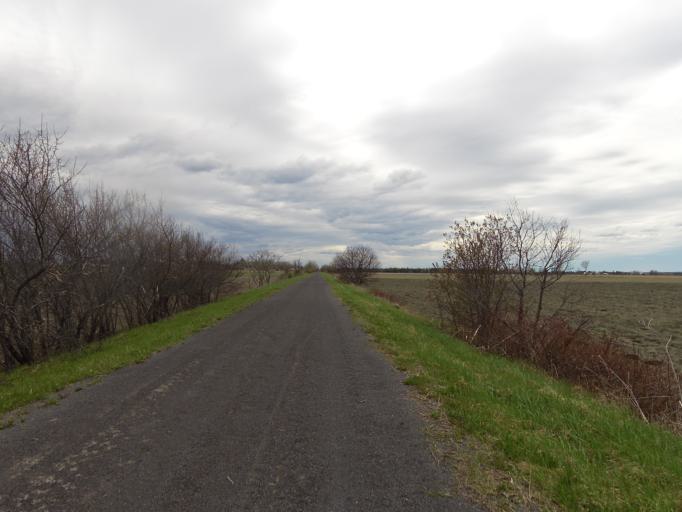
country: CA
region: Ontario
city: Hawkesbury
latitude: 45.5449
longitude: -74.7860
